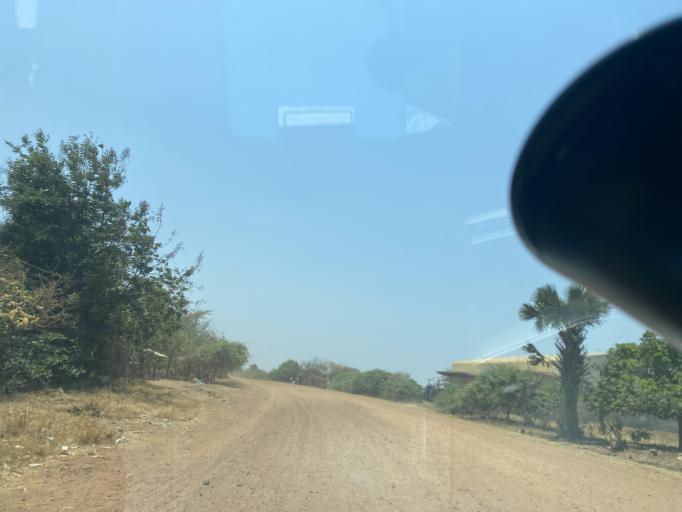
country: ZM
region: Southern
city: Nakambala
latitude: -15.4724
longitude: 27.8999
